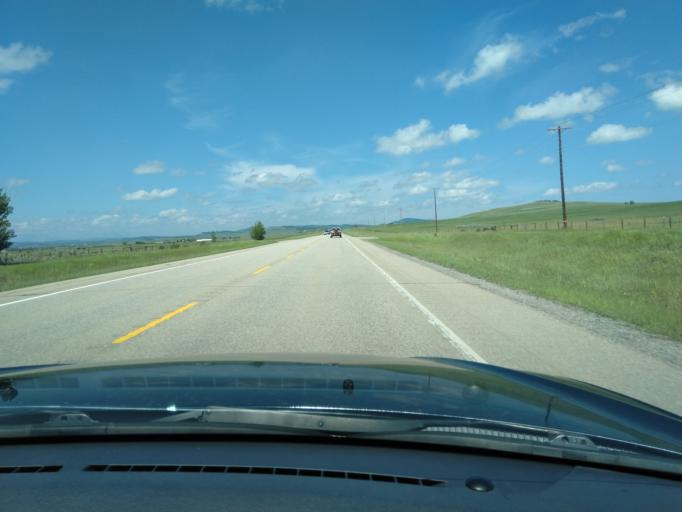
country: CA
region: Alberta
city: Cochrane
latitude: 51.2105
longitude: -114.5248
